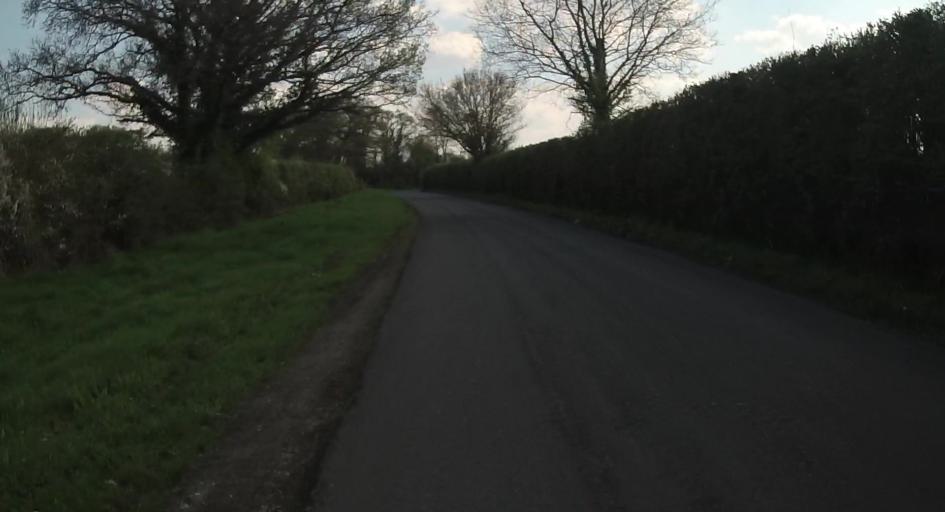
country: GB
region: England
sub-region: West Berkshire
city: Stratfield Mortimer
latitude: 51.3661
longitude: -1.0050
